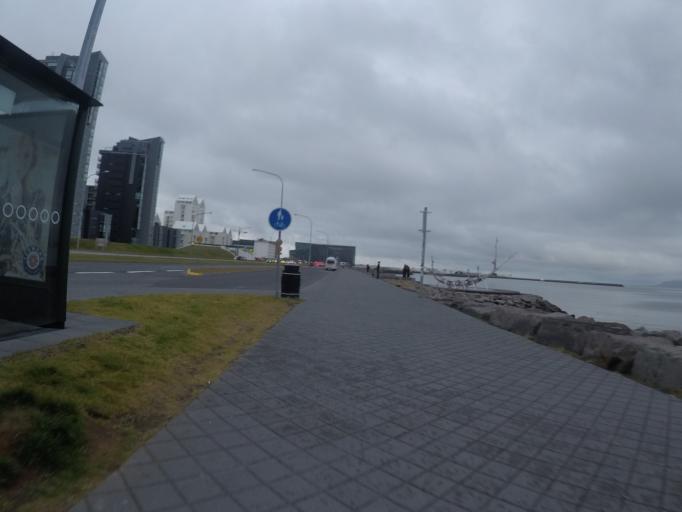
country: IS
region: Capital Region
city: Reykjavik
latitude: 64.1471
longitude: -21.9215
